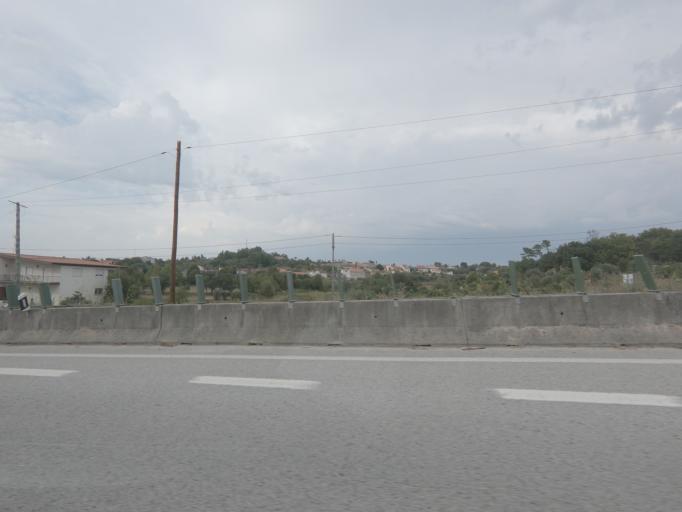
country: PT
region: Viseu
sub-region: Santa Comba Dao
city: Santa Comba Dao
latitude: 40.3854
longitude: -8.1200
